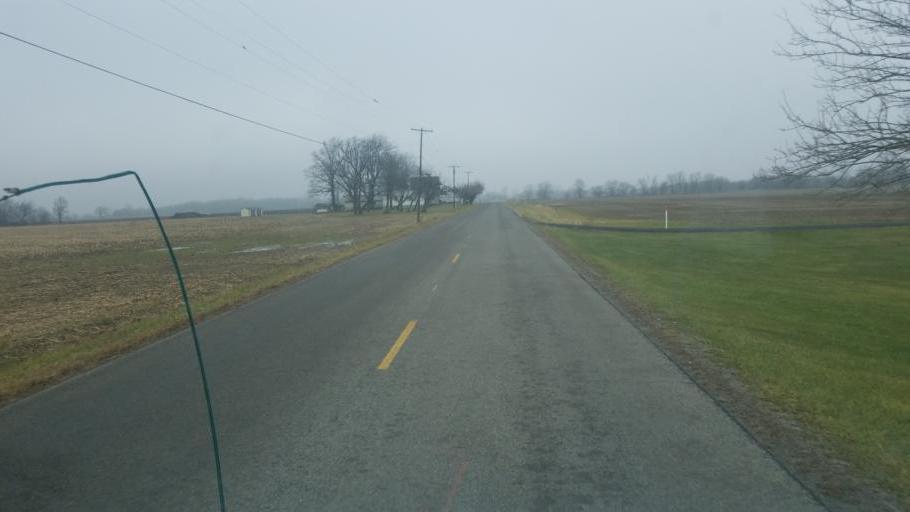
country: US
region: Ohio
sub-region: Champaign County
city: North Lewisburg
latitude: 40.3426
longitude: -83.5604
